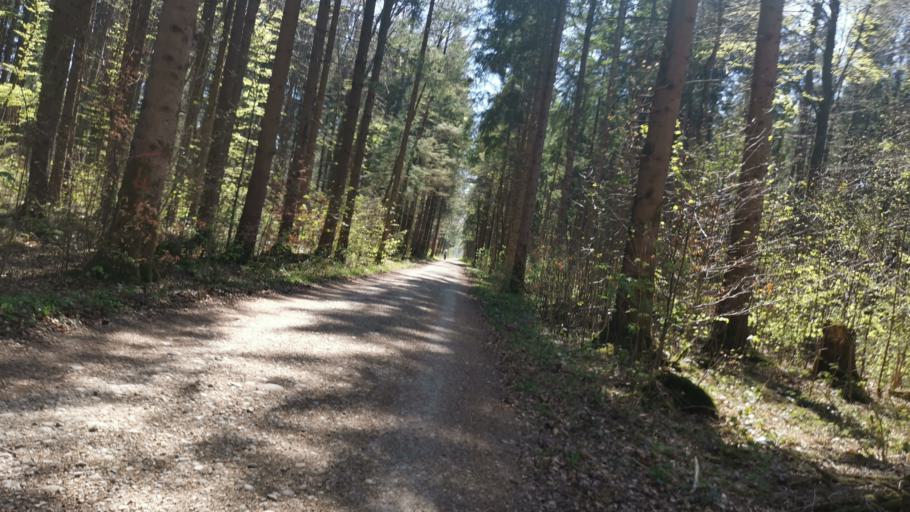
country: DE
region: Bavaria
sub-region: Upper Bavaria
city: Planegg
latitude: 48.0826
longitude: 11.4254
